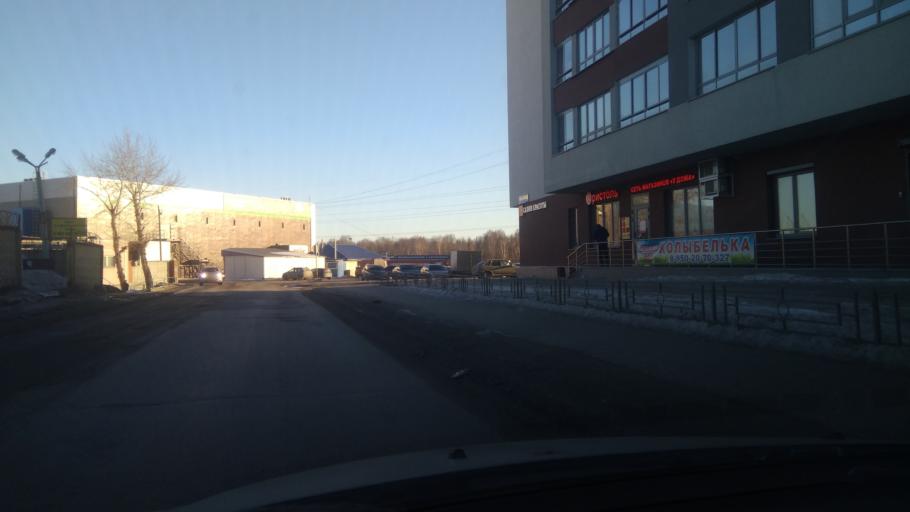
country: RU
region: Sverdlovsk
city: Istok
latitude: 56.8252
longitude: 60.6983
